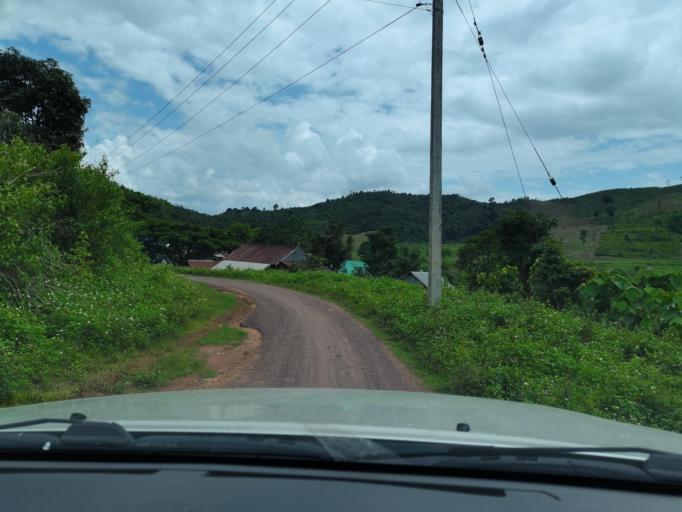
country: LA
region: Loungnamtha
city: Muang Long
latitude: 20.7066
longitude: 101.0098
